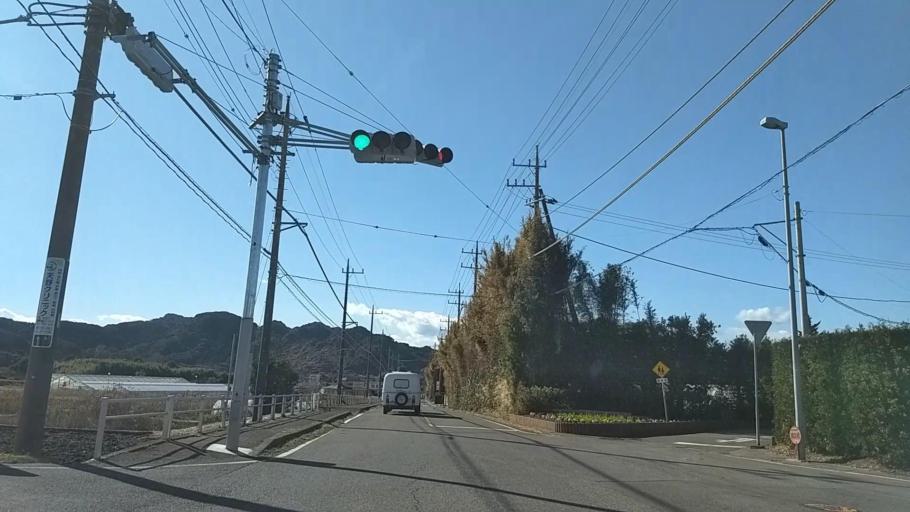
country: JP
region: Chiba
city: Tateyama
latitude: 34.9317
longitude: 139.8386
